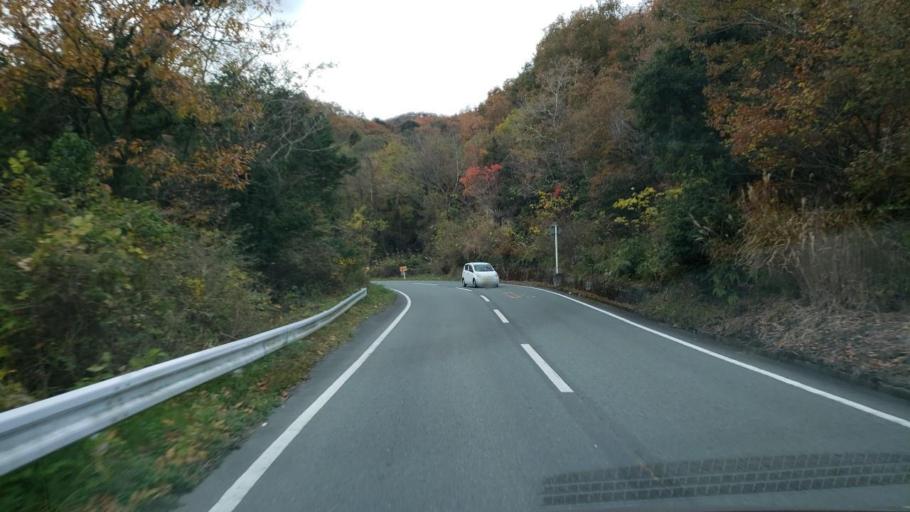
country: JP
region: Tokushima
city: Wakimachi
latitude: 34.0906
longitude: 134.2036
